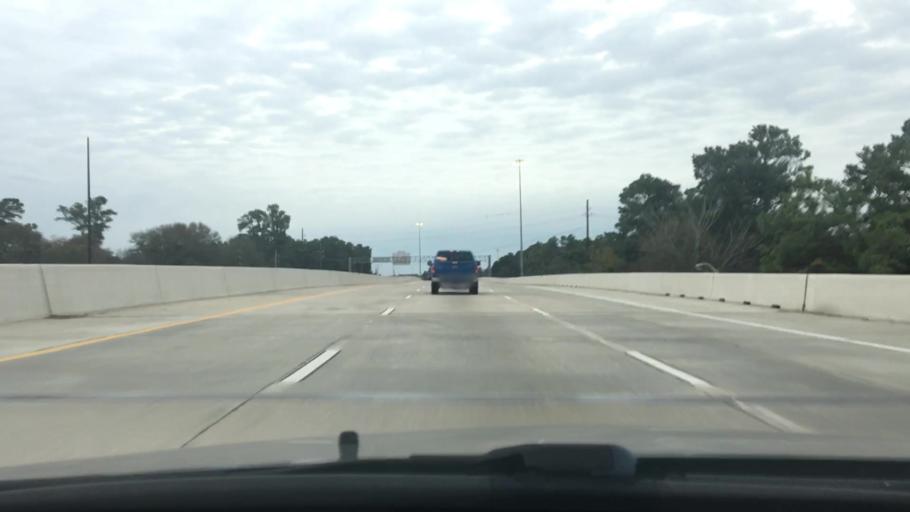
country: US
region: Texas
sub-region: Harris County
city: Spring
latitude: 30.0765
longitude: -95.4112
